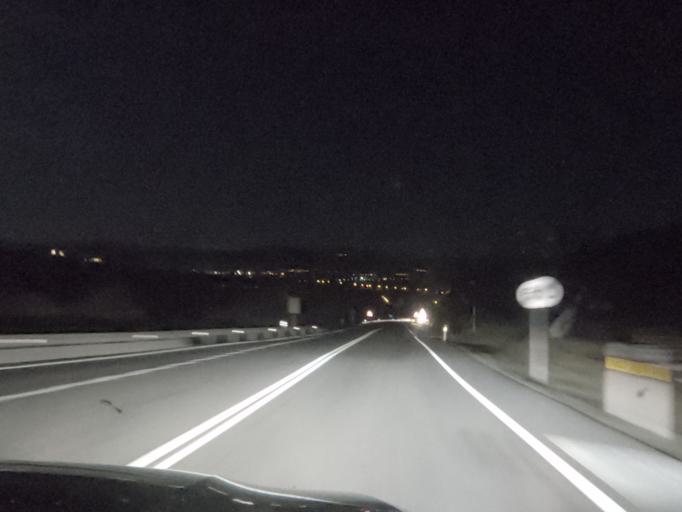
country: ES
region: Galicia
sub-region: Provincia de Ourense
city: Verin
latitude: 41.9609
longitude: -7.5054
